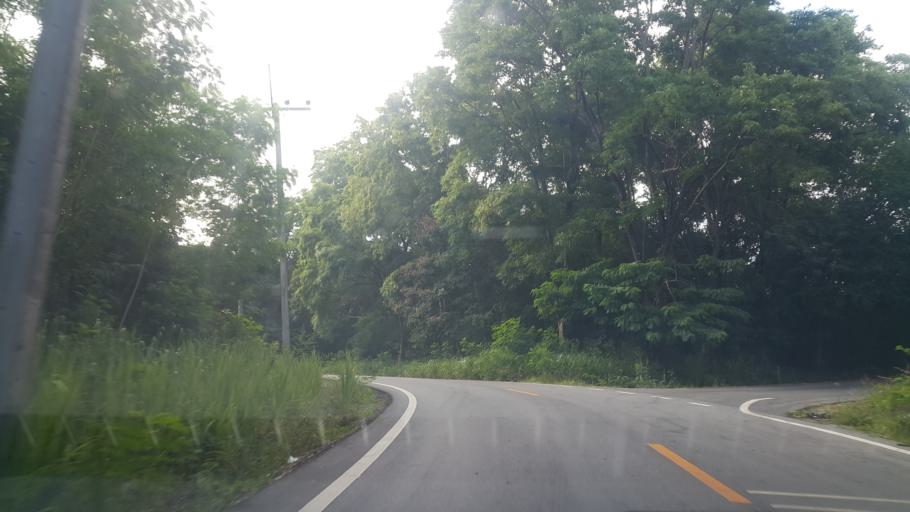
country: TH
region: Rayong
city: Ban Chang
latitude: 12.7823
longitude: 100.9653
